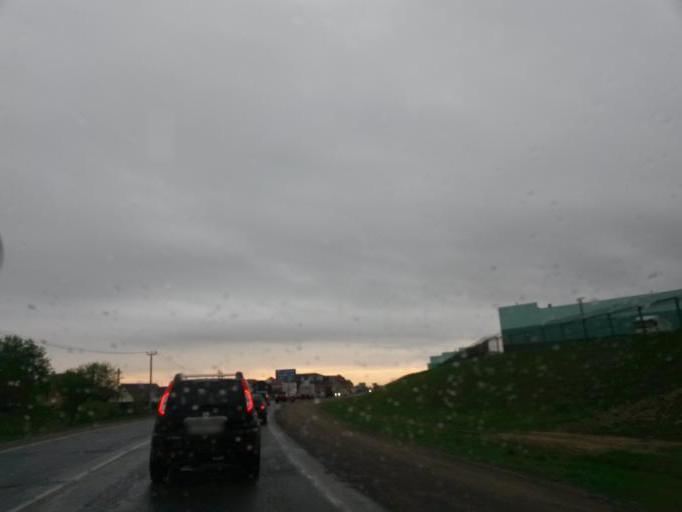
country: RU
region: Moskovskaya
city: Yam
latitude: 55.4804
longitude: 37.7210
